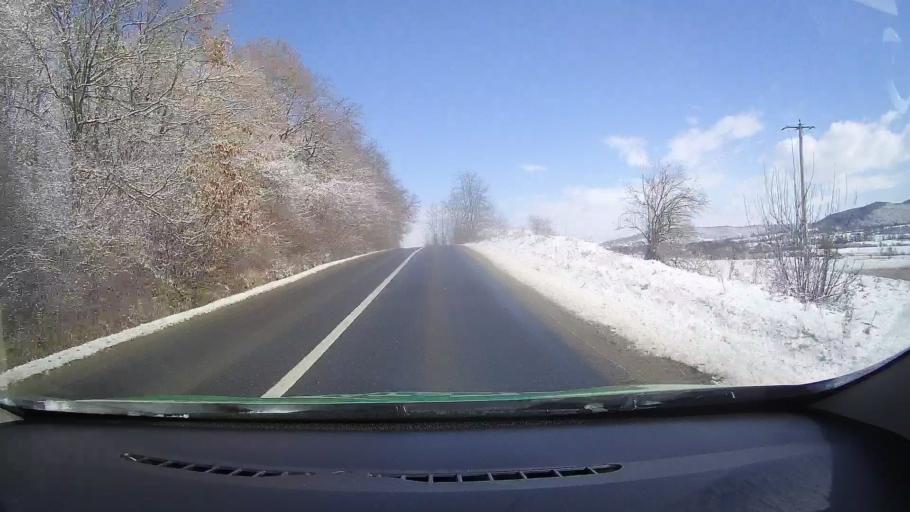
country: RO
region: Sibiu
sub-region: Comuna Rosia
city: Rosia
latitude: 45.8286
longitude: 24.3915
